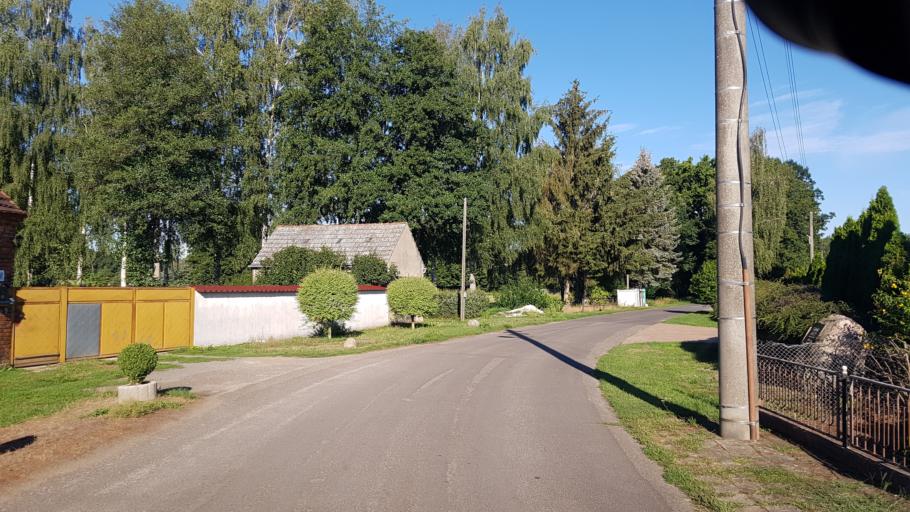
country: DE
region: Brandenburg
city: Calau
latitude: 51.7454
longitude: 13.9179
